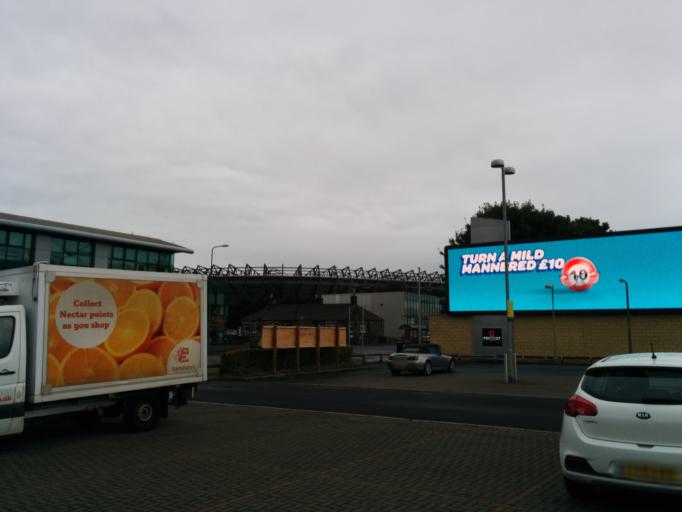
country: GB
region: Scotland
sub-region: Edinburgh
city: Colinton
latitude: 55.9387
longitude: -3.2409
